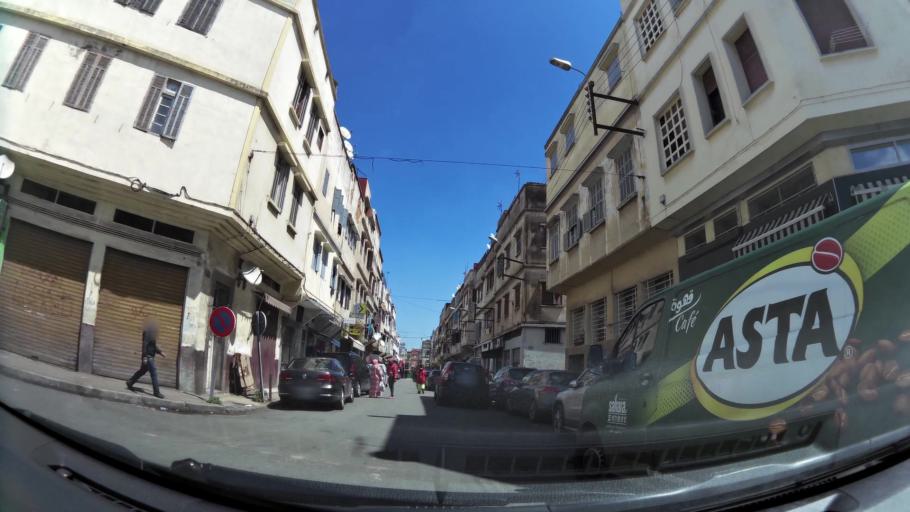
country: MA
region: Grand Casablanca
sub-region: Casablanca
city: Casablanca
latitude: 33.5675
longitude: -7.6041
